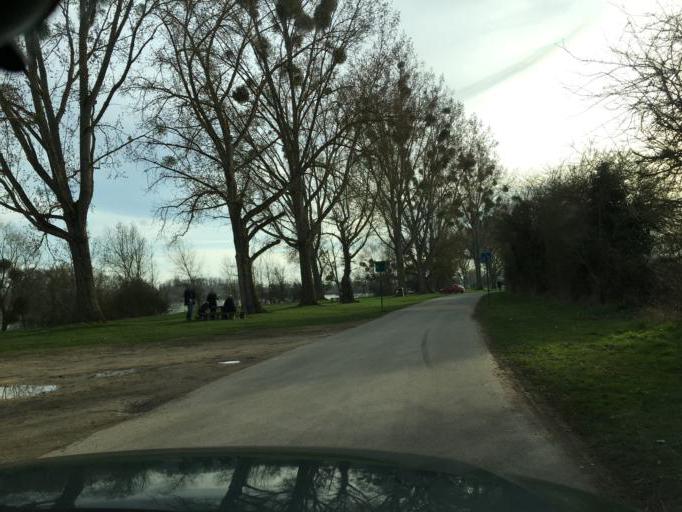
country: FR
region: Centre
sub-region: Departement du Loiret
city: Beaugency
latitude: 47.7851
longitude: 1.6470
